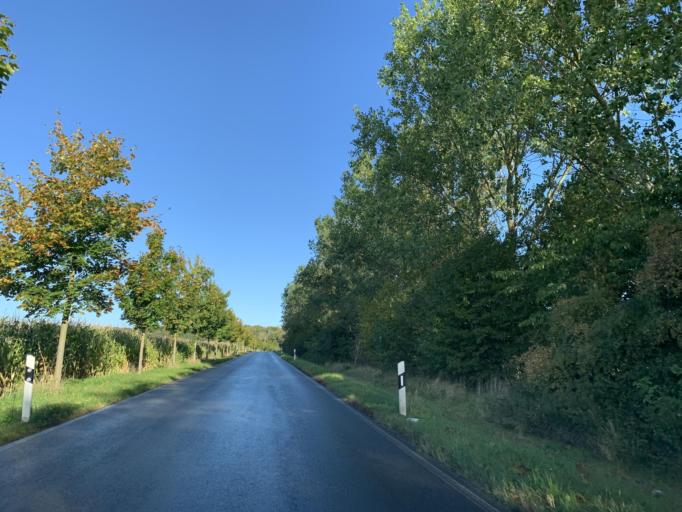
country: DE
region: Mecklenburg-Vorpommern
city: Burg Stargard
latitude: 53.4924
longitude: 13.2669
